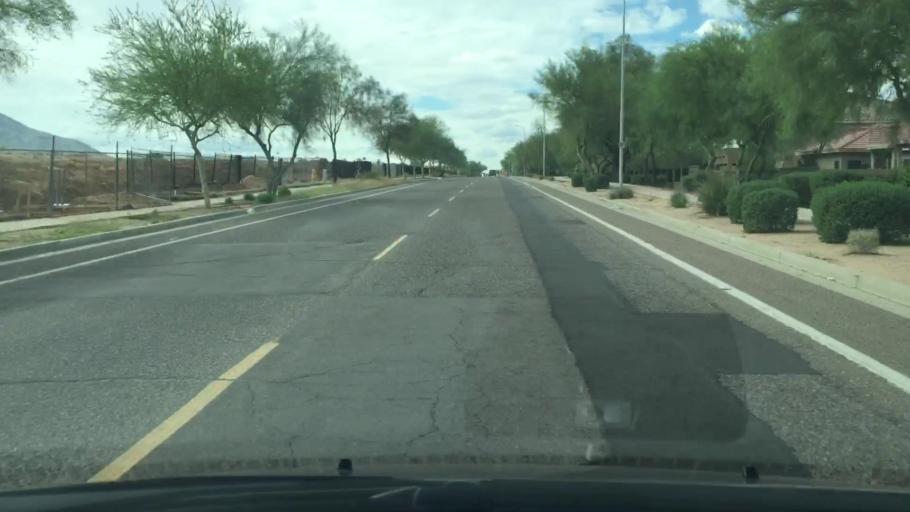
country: US
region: Arizona
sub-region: Maricopa County
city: Phoenix
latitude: 33.3633
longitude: -112.0566
